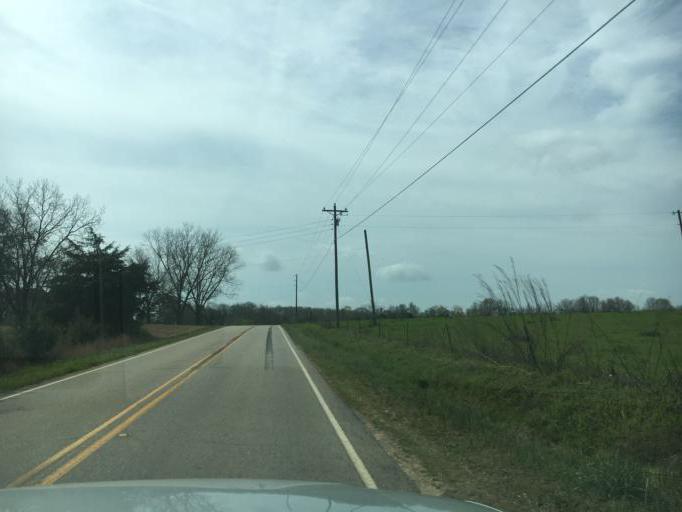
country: US
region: Georgia
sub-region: Hart County
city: Royston
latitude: 34.3477
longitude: -83.0413
